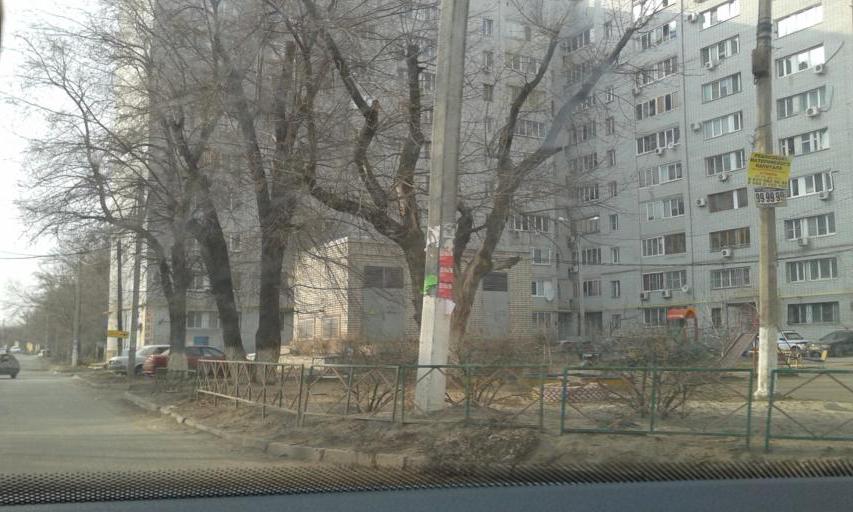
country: RU
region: Volgograd
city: Volgograd
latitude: 48.6554
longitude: 44.4305
